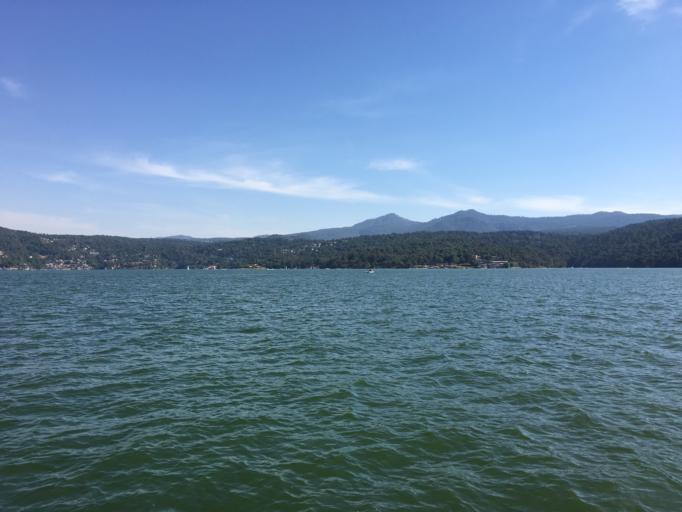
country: MX
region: Mexico
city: Valle de Bravo
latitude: 19.1893
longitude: -100.1497
